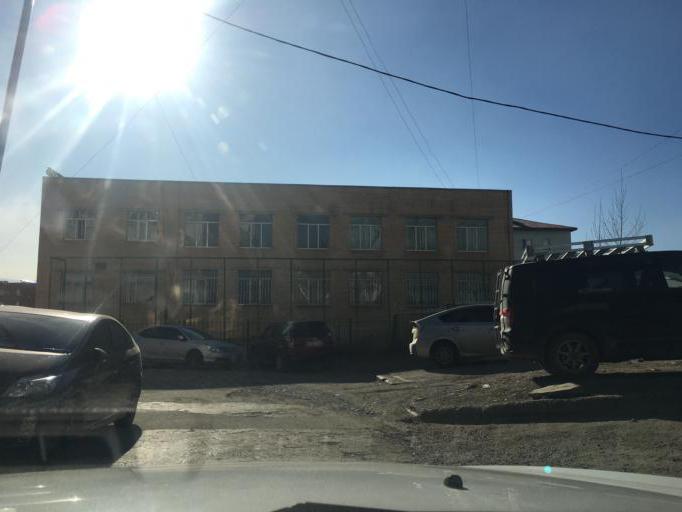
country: MN
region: Ulaanbaatar
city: Ulaanbaatar
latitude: 47.9202
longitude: 106.8657
